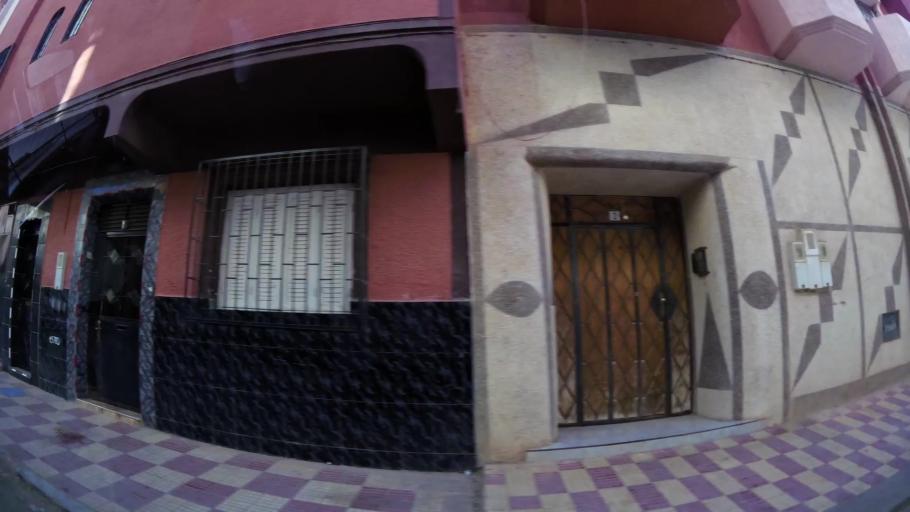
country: MA
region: Oriental
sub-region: Berkane-Taourirt
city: Berkane
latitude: 34.9322
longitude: -2.3397
